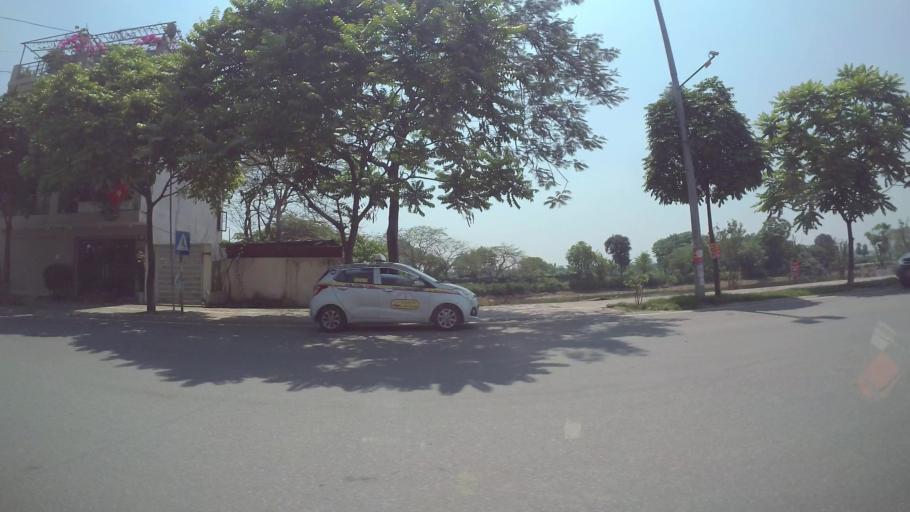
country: VN
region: Ha Noi
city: Hoan Kiem
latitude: 21.0376
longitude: 105.8821
